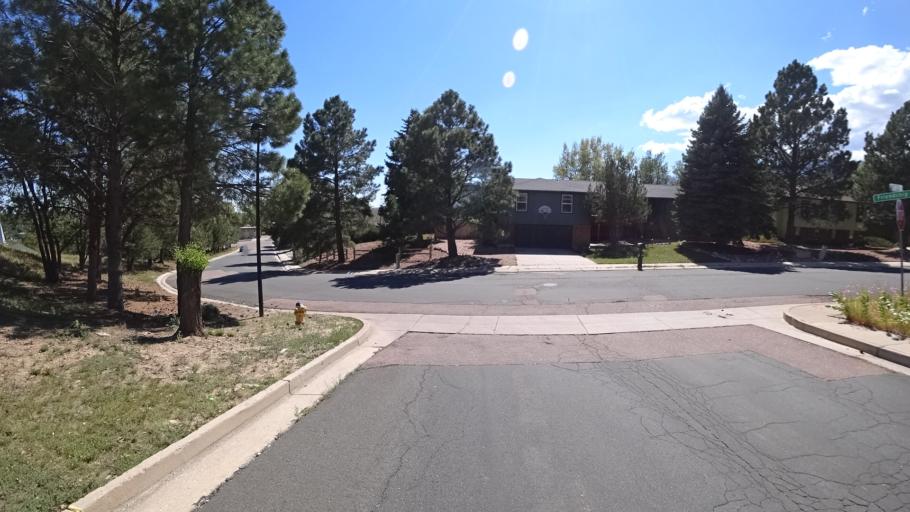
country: US
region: Colorado
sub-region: El Paso County
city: Colorado Springs
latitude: 38.8571
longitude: -104.8541
